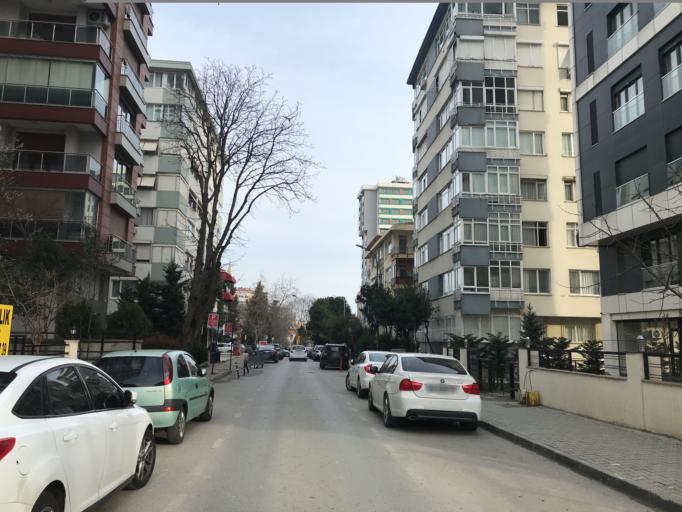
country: TR
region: Istanbul
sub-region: Atasehir
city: Atasehir
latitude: 40.9557
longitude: 29.0920
